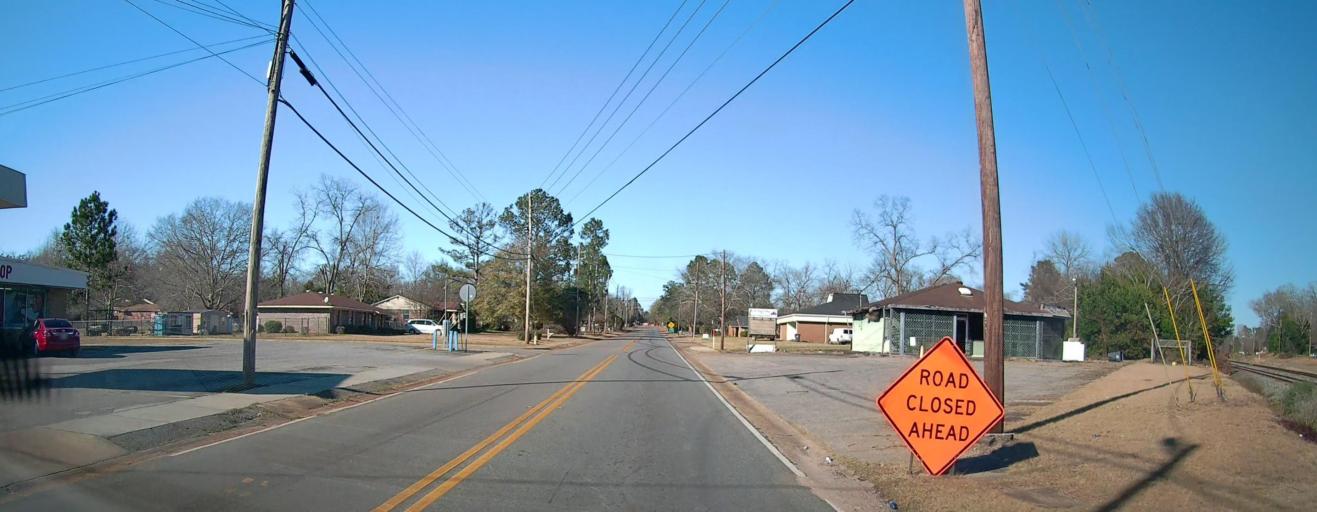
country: US
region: Georgia
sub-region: Sumter County
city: Americus
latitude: 32.0810
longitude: -84.2320
